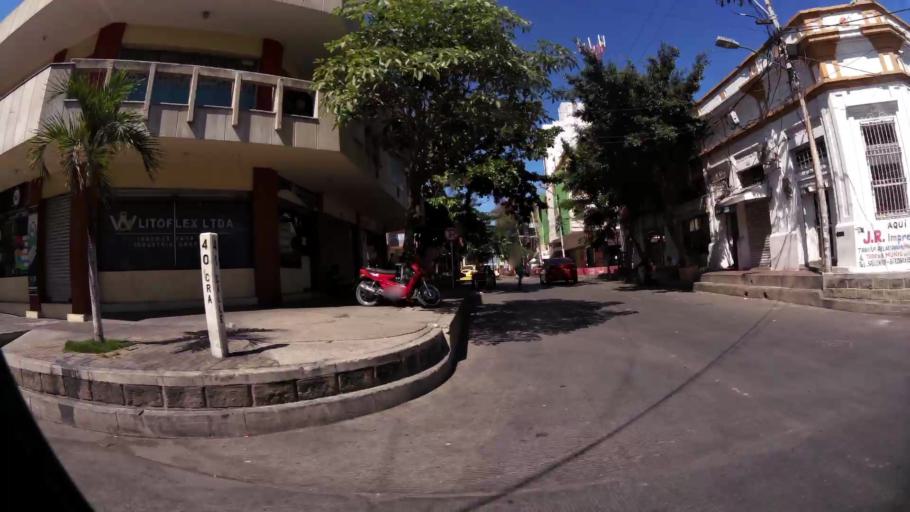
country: CO
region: Atlantico
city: Barranquilla
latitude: 10.9805
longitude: -74.7832
